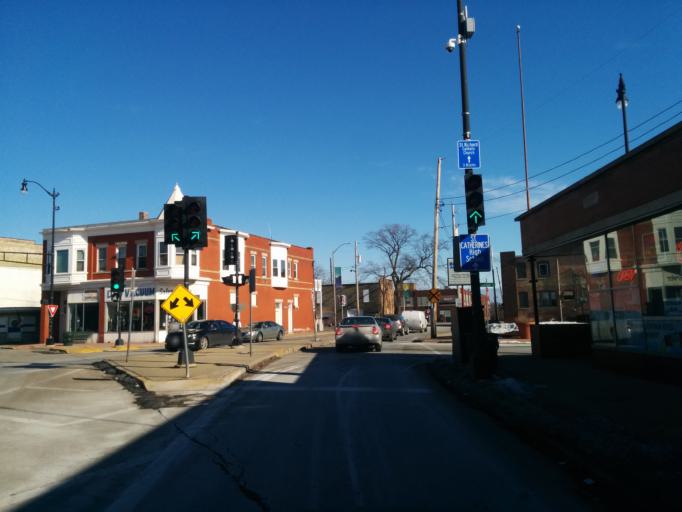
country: US
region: Wisconsin
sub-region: Racine County
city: Racine
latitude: 42.7153
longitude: -87.7970
